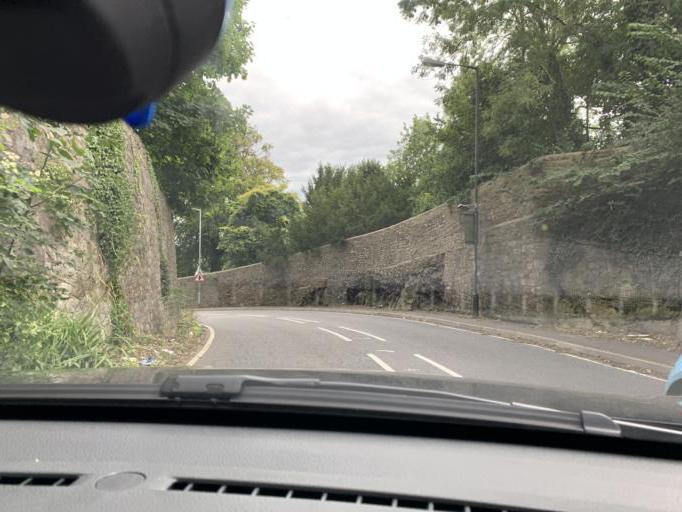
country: GB
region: England
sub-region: North Somerset
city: Easton-in-Gordano
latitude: 51.4925
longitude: -2.6574
